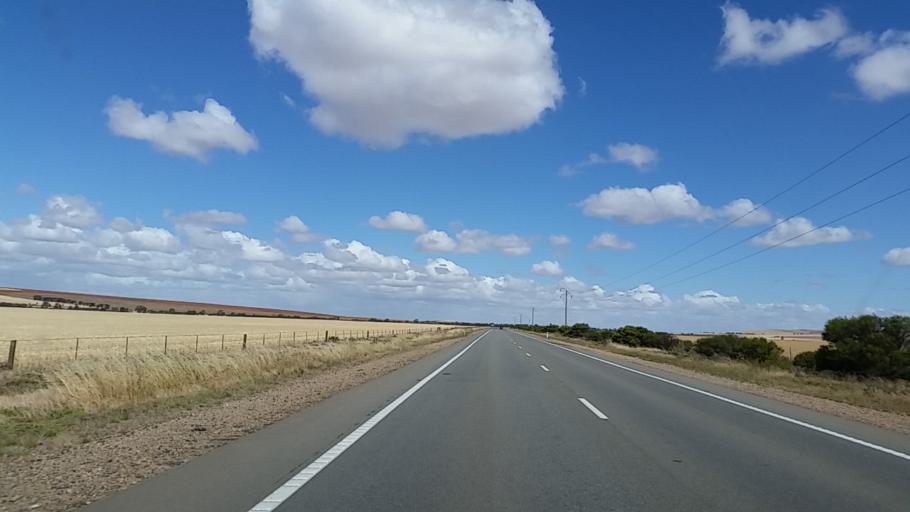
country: AU
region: South Australia
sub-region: Port Pirie City and Dists
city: Crystal Brook
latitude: -33.4832
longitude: 138.1737
